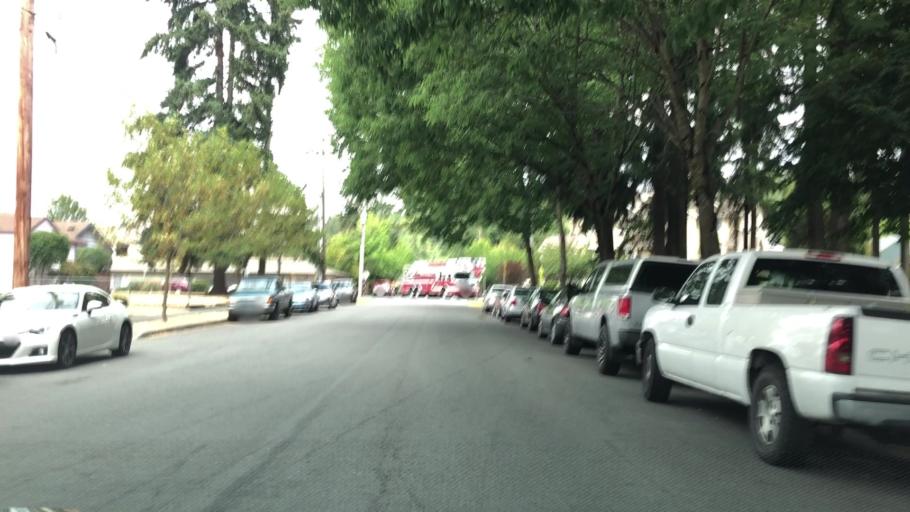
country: US
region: Washington
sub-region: King County
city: Redmond
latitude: 47.6730
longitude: -122.1162
